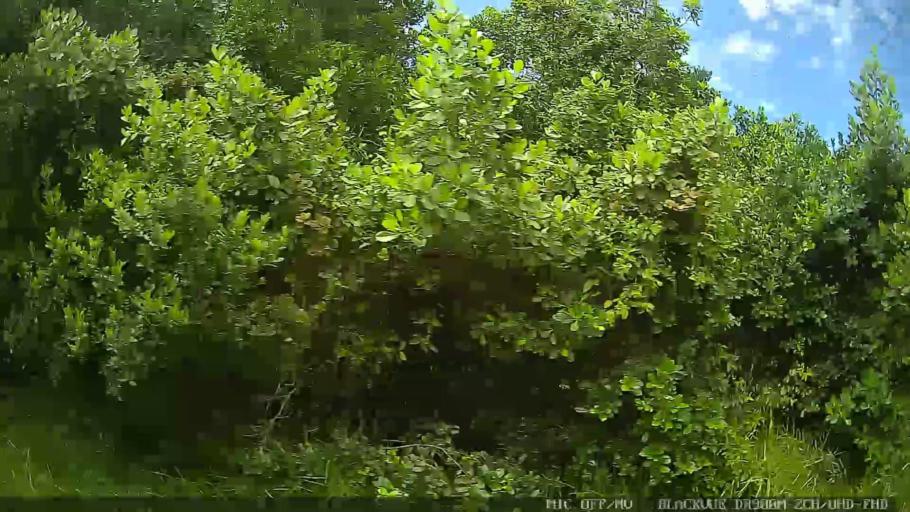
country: BR
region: Sao Paulo
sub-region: Iguape
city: Iguape
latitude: -24.7206
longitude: -47.5277
